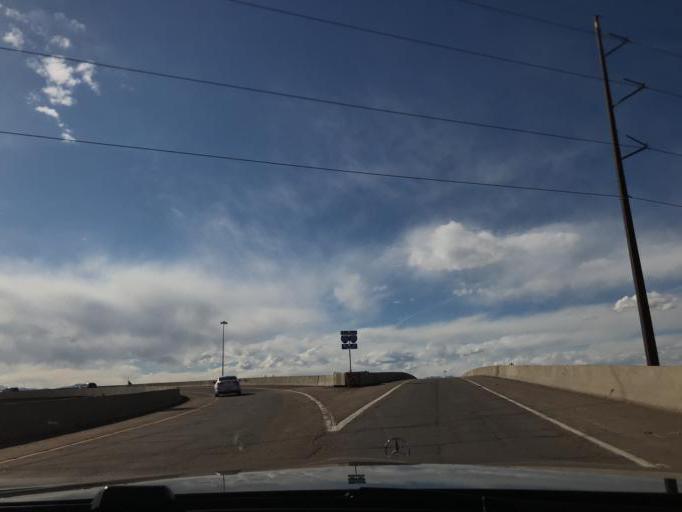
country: US
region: Colorado
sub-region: Denver County
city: Denver
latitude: 39.7260
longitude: -105.0106
